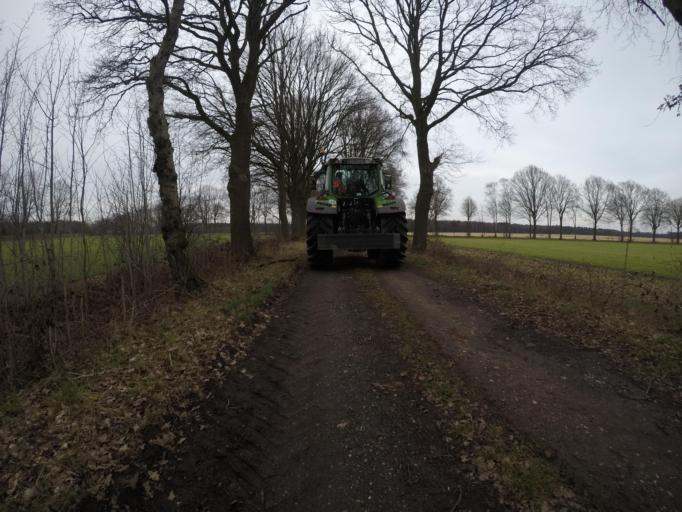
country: DE
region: North Rhine-Westphalia
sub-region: Regierungsbezirk Munster
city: Rhede
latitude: 51.7617
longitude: 6.6733
